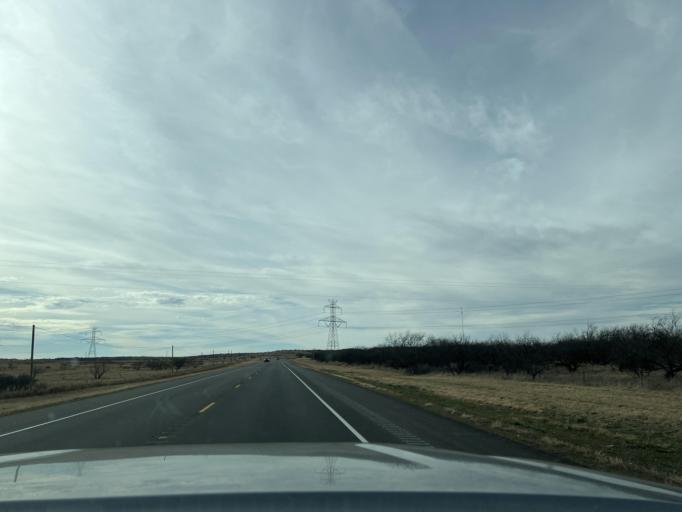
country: US
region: Texas
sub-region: Shackelford County
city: Albany
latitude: 32.7054
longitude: -99.4007
